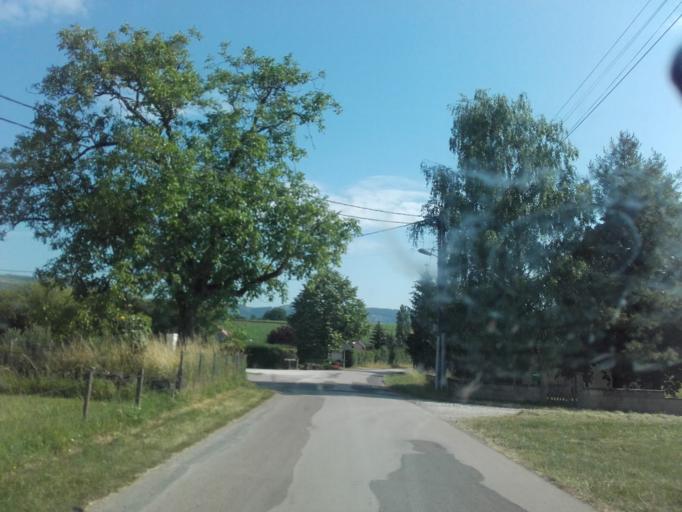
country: FR
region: Bourgogne
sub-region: Departement de Saone-et-Loire
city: Saint-Leger-sur-Dheune
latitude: 46.8954
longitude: 4.6747
